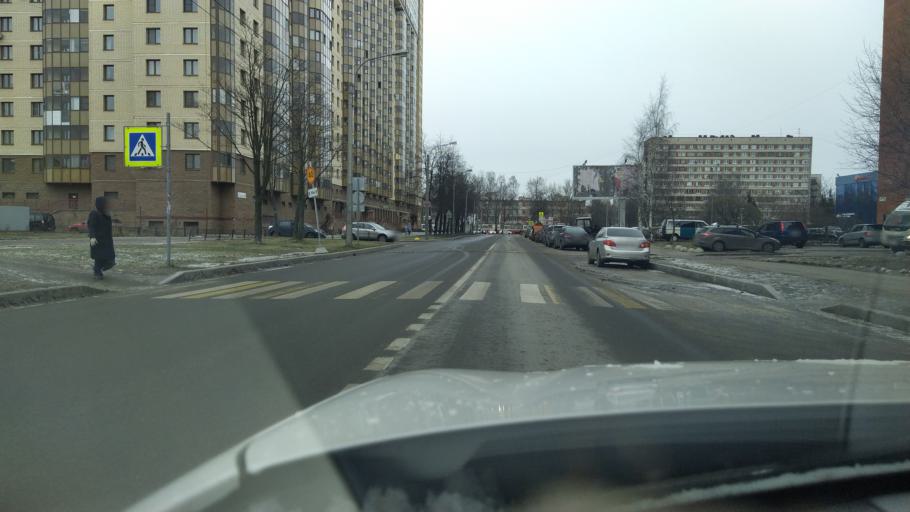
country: RU
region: Leningrad
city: Akademicheskoe
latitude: 60.0092
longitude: 30.4041
